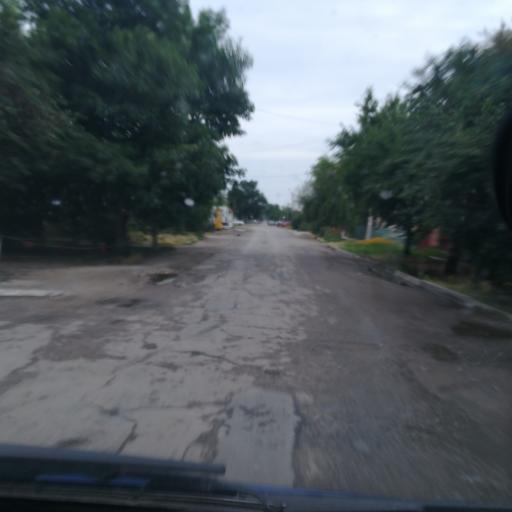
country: RU
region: Krasnodarskiy
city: Slavyansk-na-Kubani
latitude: 45.2615
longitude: 38.1274
